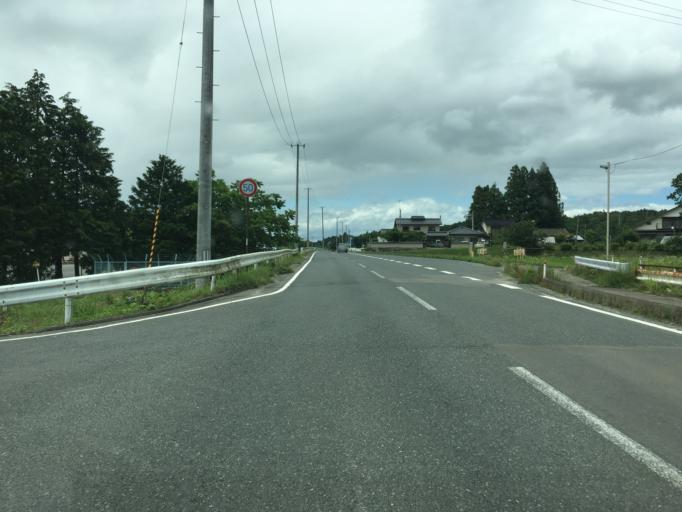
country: JP
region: Miyagi
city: Marumori
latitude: 37.7292
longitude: 140.9291
